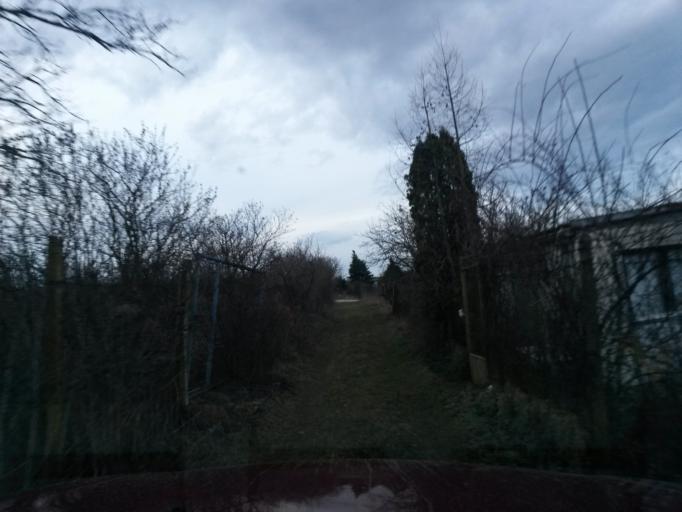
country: SK
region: Kosicky
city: Kosice
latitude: 48.7274
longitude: 21.3080
